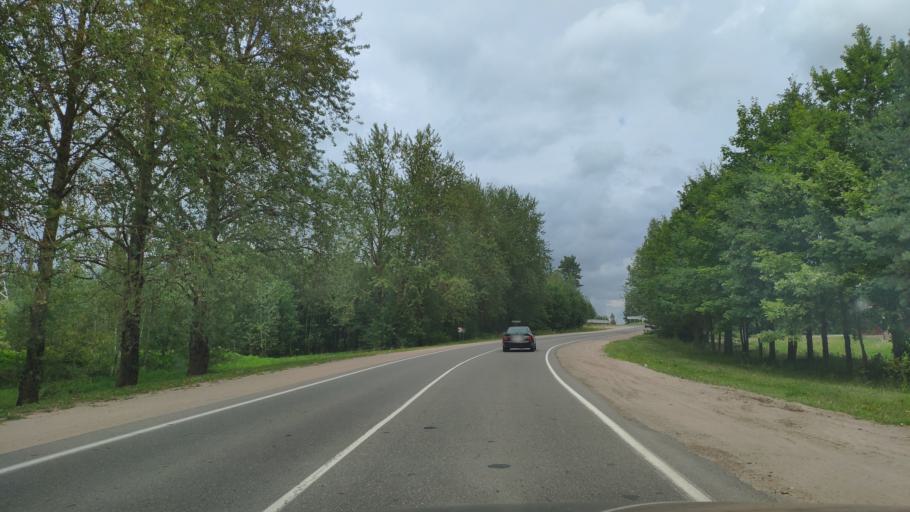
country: BY
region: Minsk
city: Zaslawye
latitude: 53.9873
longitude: 27.2581
